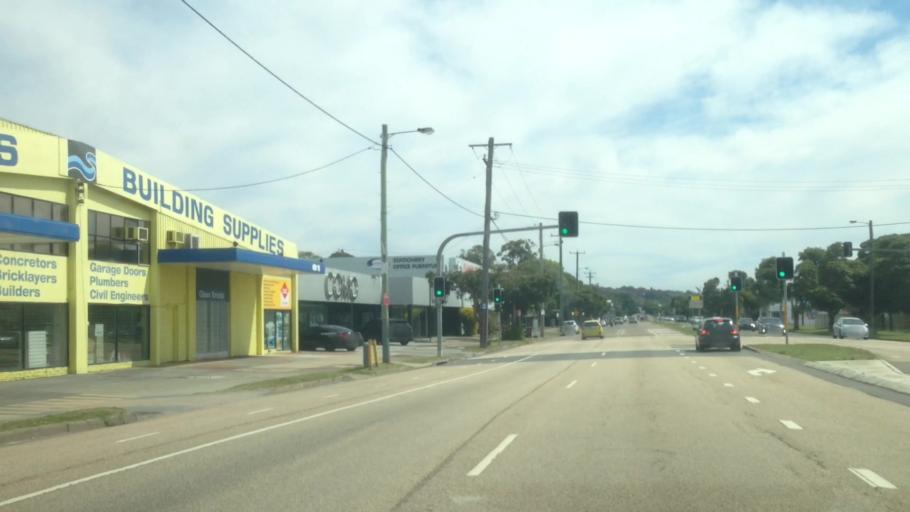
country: AU
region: New South Wales
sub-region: Newcastle
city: Broadmeadow
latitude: -32.9242
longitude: 151.7312
